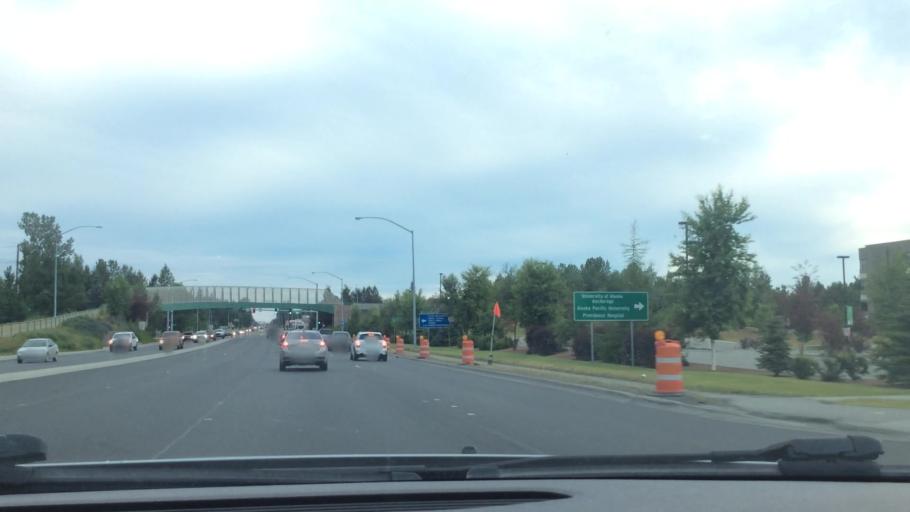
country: US
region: Alaska
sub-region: Anchorage Municipality
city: Anchorage
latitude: 61.1808
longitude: -149.8042
